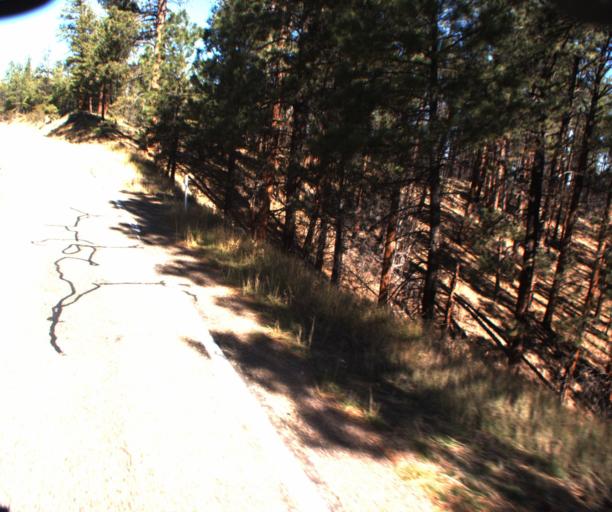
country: US
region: Arizona
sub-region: Coconino County
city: Fredonia
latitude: 36.7409
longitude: -112.2298
